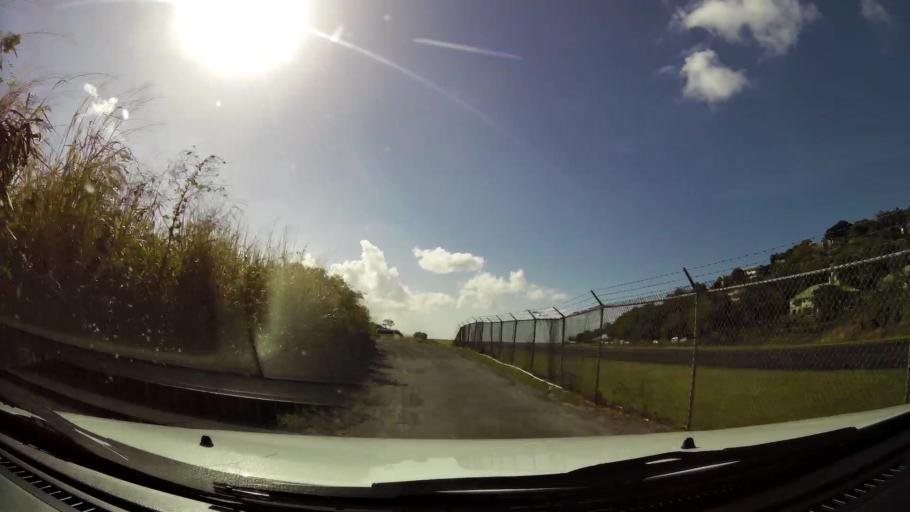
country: LC
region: Castries Quarter
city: Bisee
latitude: 14.0184
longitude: -60.9974
